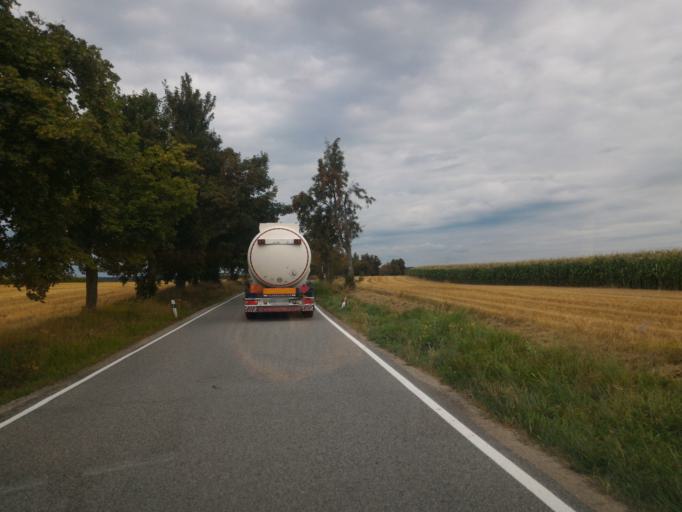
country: CZ
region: Vysocina
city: Zeletava
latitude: 49.1701
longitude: 15.5873
